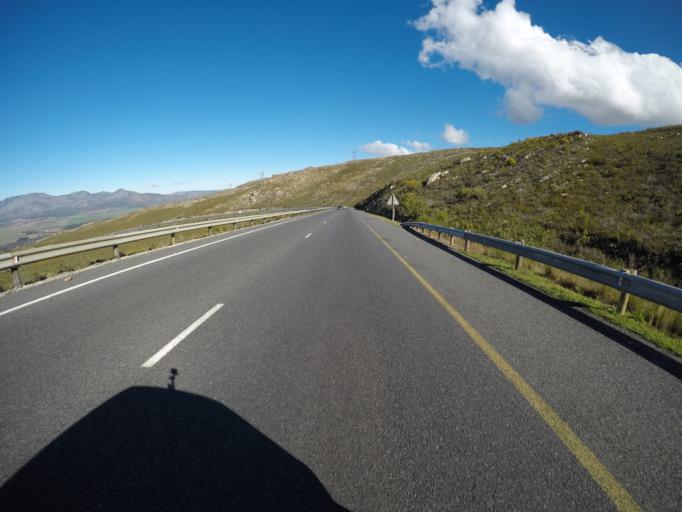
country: ZA
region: Western Cape
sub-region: Overberg District Municipality
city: Grabouw
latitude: -34.2211
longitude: 19.1727
